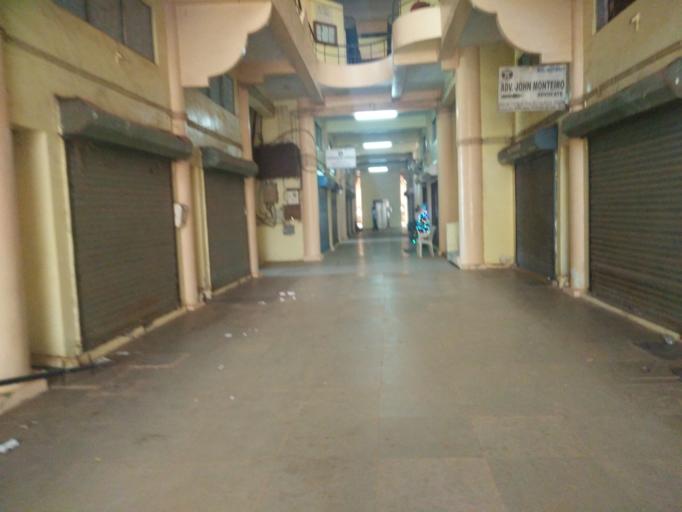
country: IN
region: Goa
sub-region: South Goa
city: Madgaon
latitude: 15.2848
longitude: 73.9579
